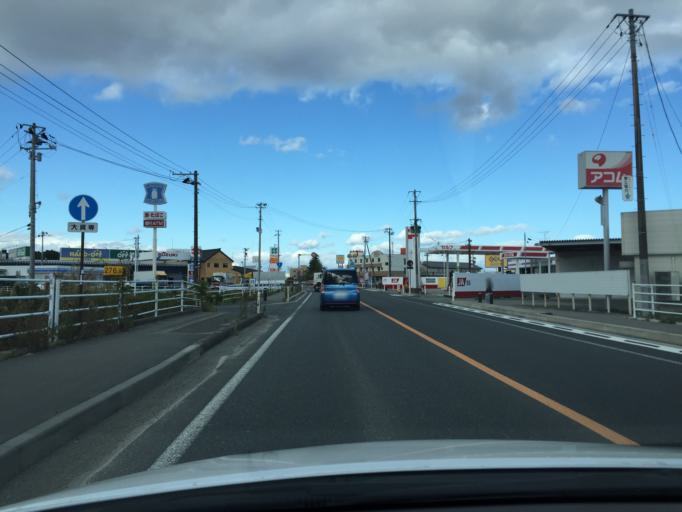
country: JP
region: Fukushima
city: Namie
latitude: 37.6271
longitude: 140.9904
